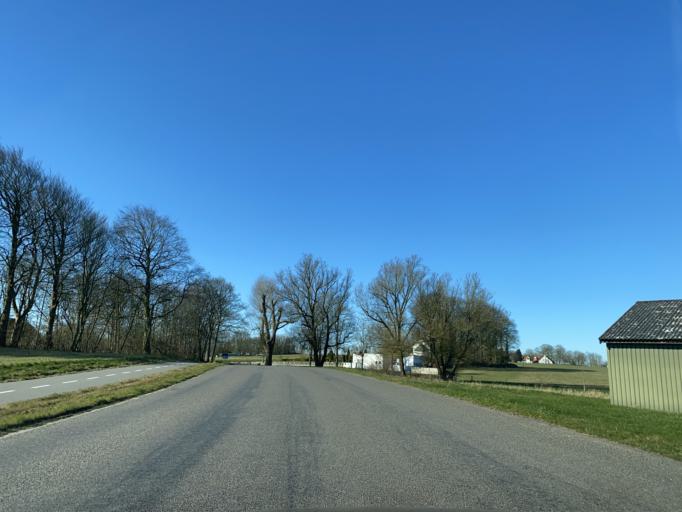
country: DK
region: Central Jutland
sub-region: Skanderborg Kommune
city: Skovby
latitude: 56.1948
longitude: 9.9666
